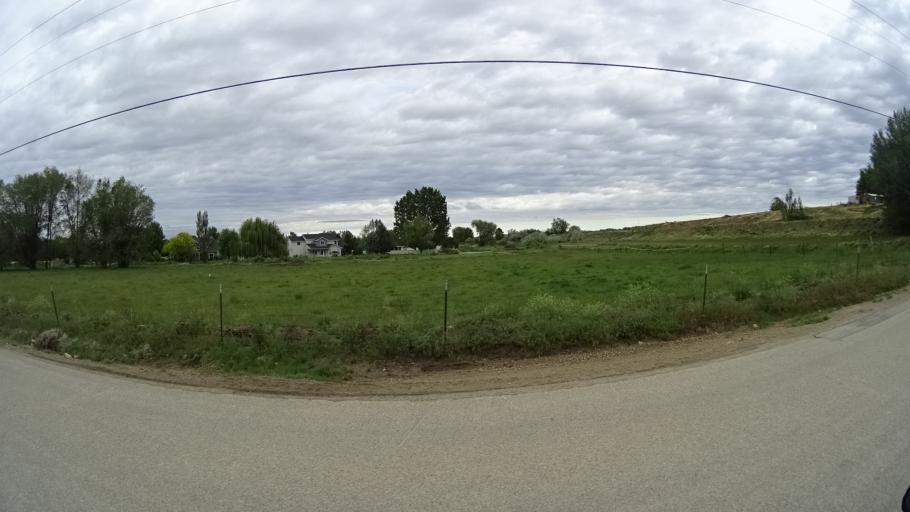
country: US
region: Idaho
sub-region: Ada County
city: Star
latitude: 43.7098
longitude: -116.4882
